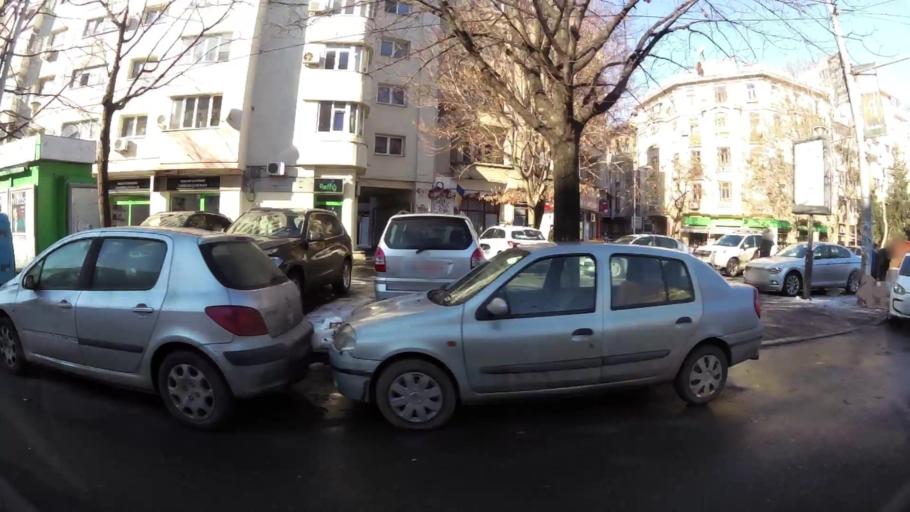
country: RO
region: Bucuresti
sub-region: Municipiul Bucuresti
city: Bucharest
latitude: 44.4390
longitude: 26.1152
